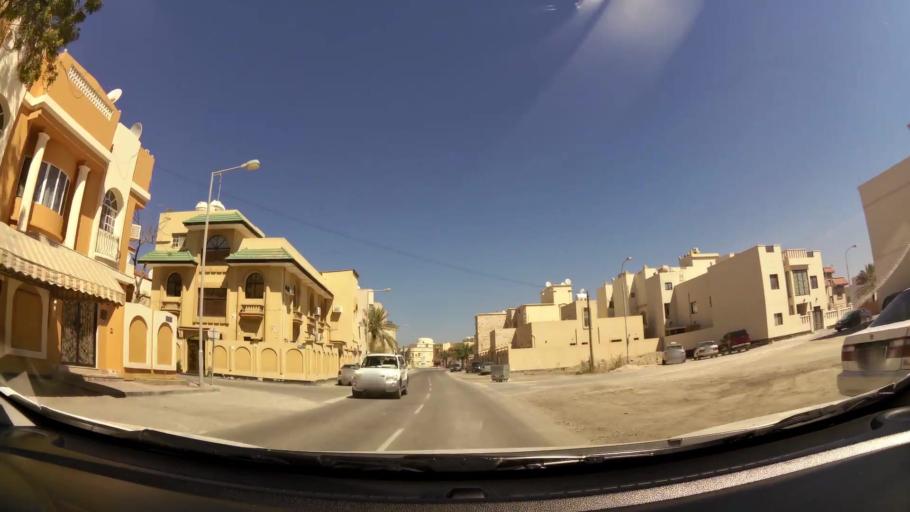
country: BH
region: Muharraq
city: Al Muharraq
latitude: 26.2783
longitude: 50.6367
